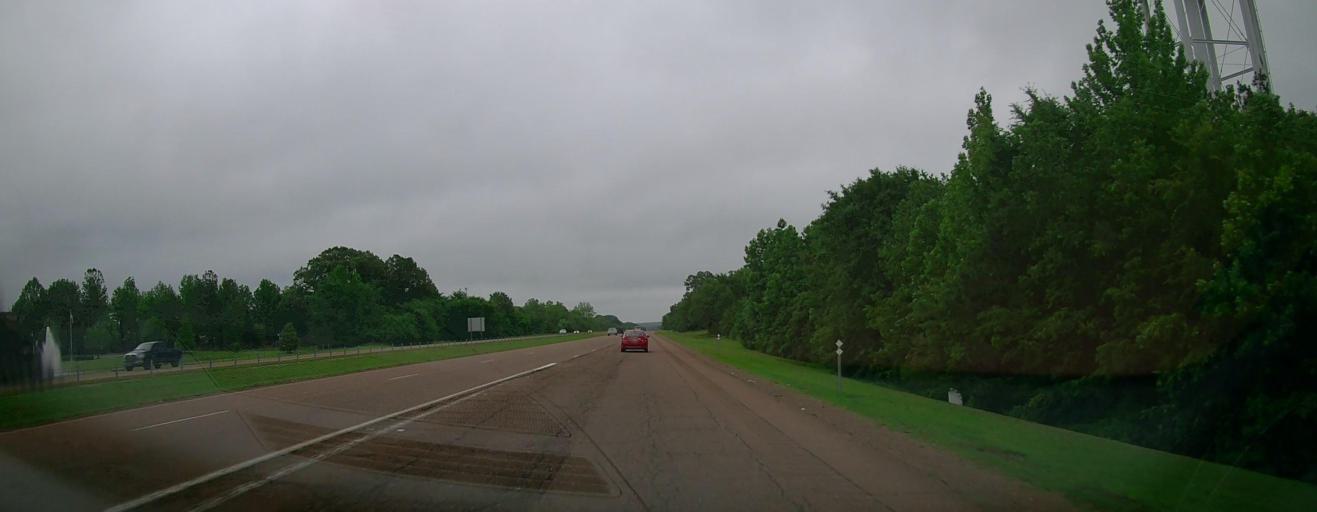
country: US
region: Mississippi
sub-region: De Soto County
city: Olive Branch
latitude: 34.9251
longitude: -89.7918
